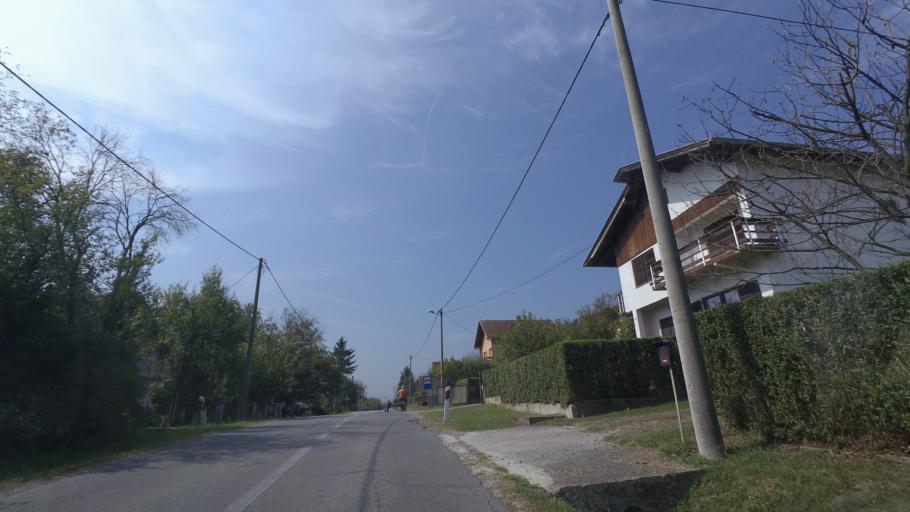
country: BA
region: Republika Srpska
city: Dobrljin
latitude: 45.1534
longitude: 16.4625
